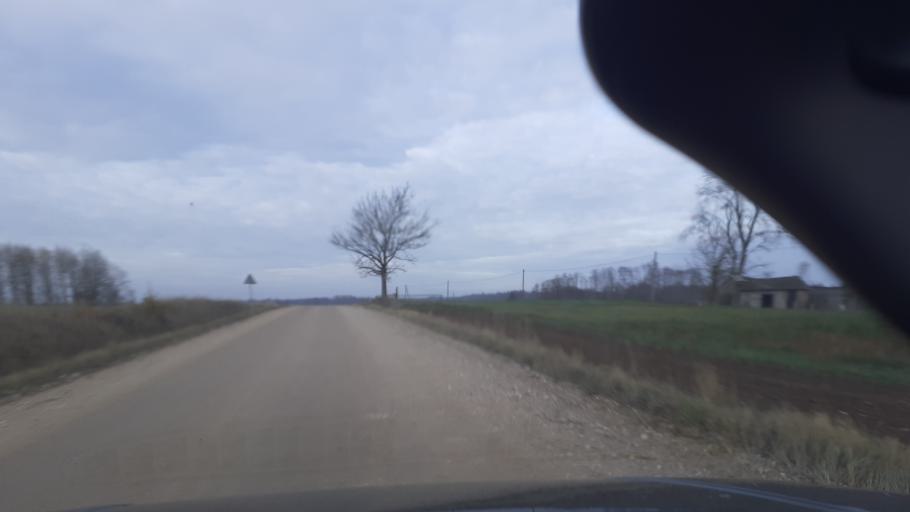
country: LV
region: Alsunga
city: Alsunga
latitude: 56.9027
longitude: 21.6558
